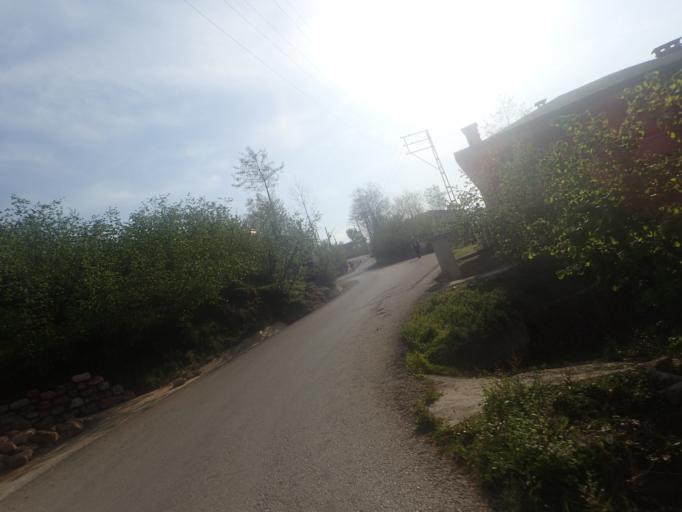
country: TR
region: Ordu
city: Catalpinar
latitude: 40.8810
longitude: 37.4832
